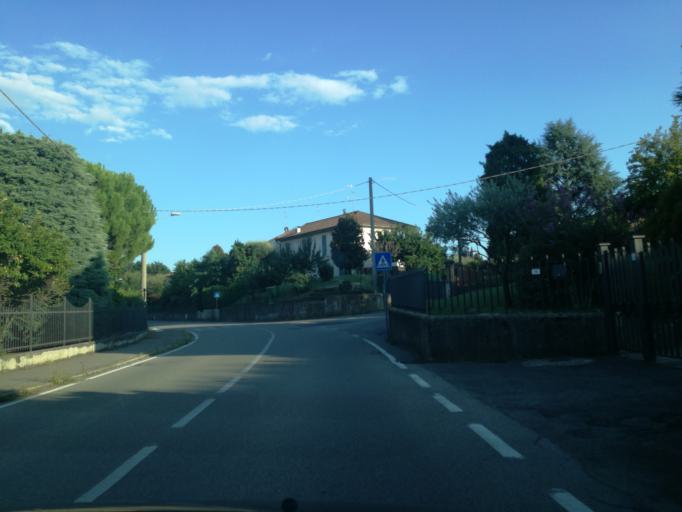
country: IT
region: Lombardy
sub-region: Provincia di Lecco
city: Paderno d'Adda
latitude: 45.6783
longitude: 9.4477
